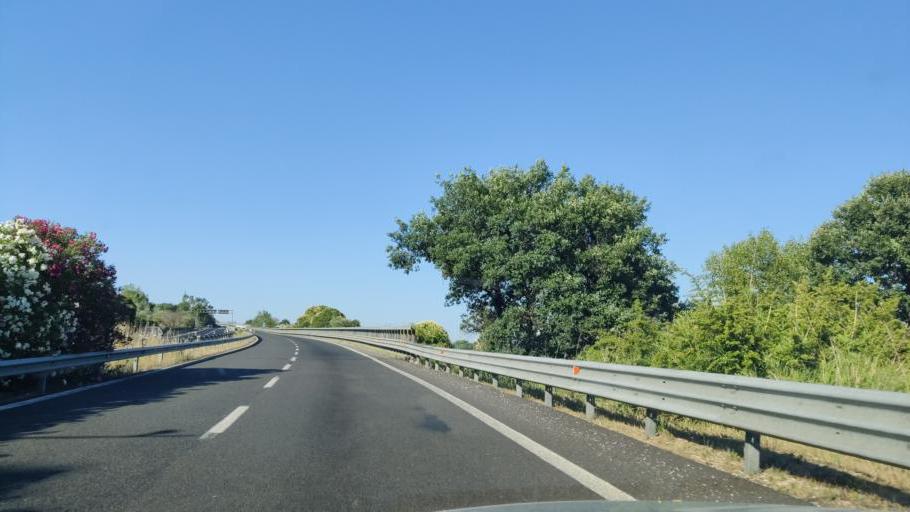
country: IT
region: Latium
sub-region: Provincia di Viterbo
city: Orte Scalo
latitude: 42.4541
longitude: 12.4051
